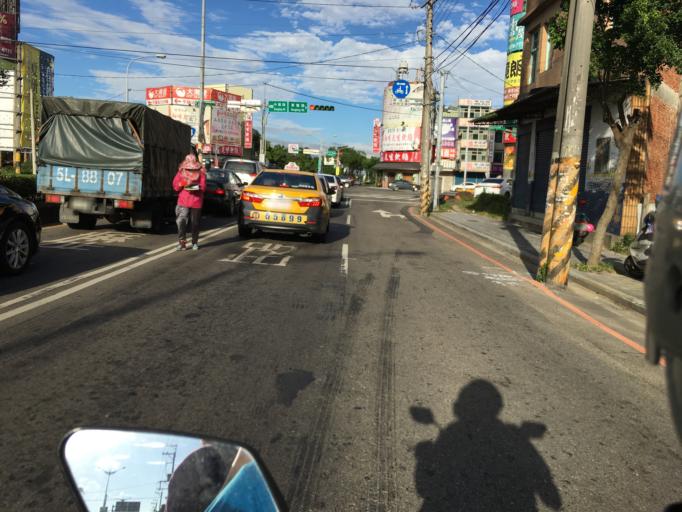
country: TW
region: Taiwan
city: Daxi
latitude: 24.8691
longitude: 121.2135
